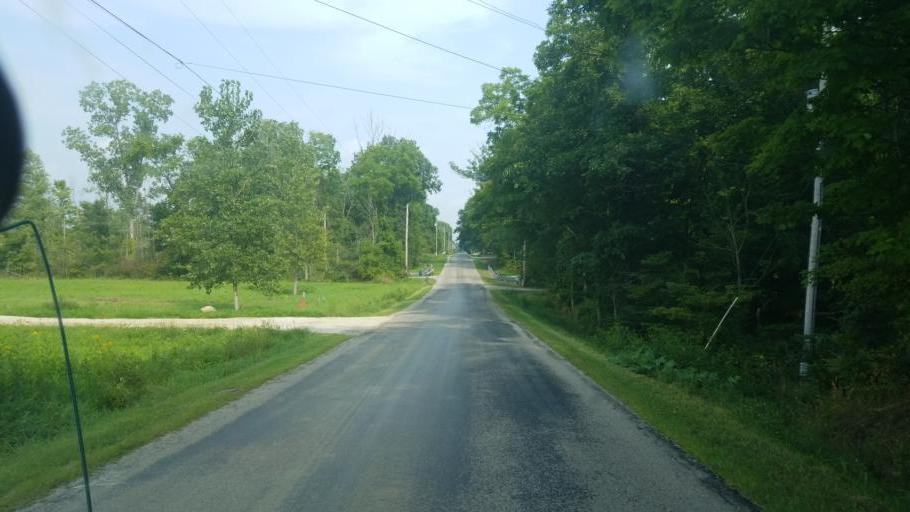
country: US
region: Ohio
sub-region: Lorain County
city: Wellington
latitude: 41.1296
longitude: -82.1465
